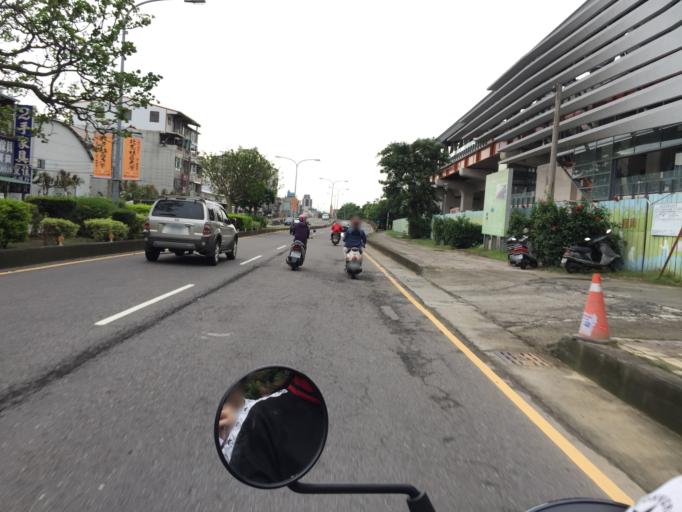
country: TW
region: Taiwan
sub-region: Taichung City
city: Taichung
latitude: 24.1496
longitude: 120.6981
